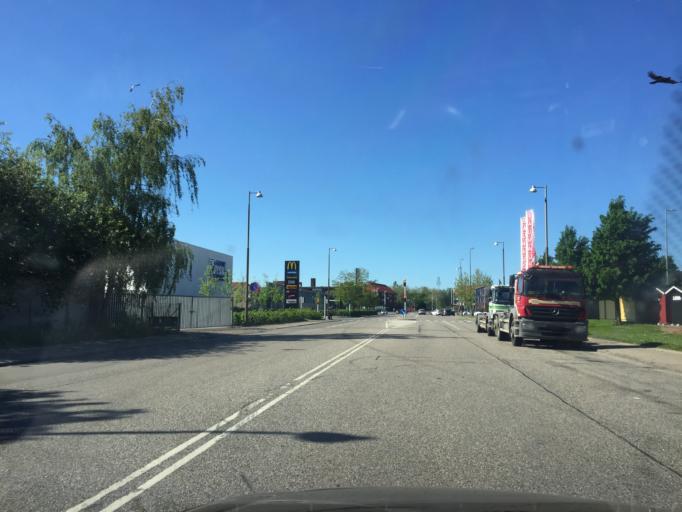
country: DK
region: Capital Region
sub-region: Albertslund Kommune
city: Albertslund
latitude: 55.6627
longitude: 12.3809
